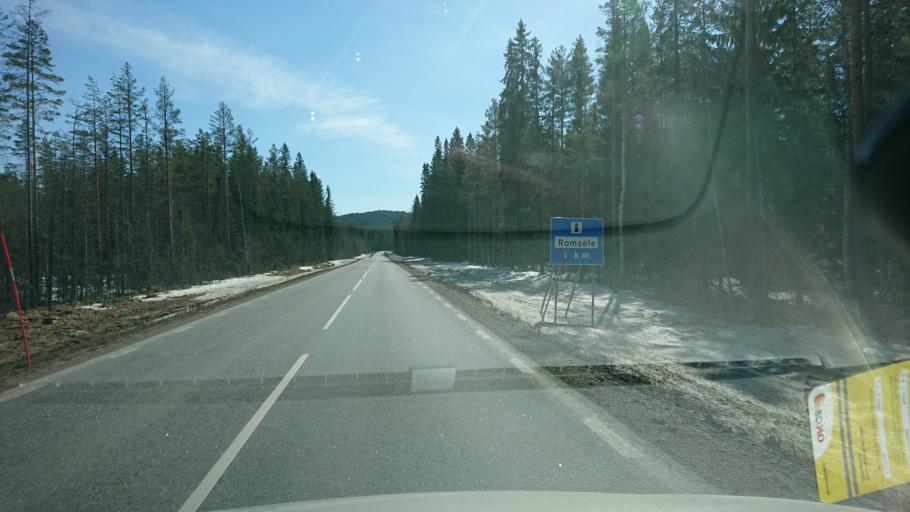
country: SE
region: Vaesternorrland
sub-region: Solleftea Kommun
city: As
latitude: 63.5730
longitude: 16.4458
